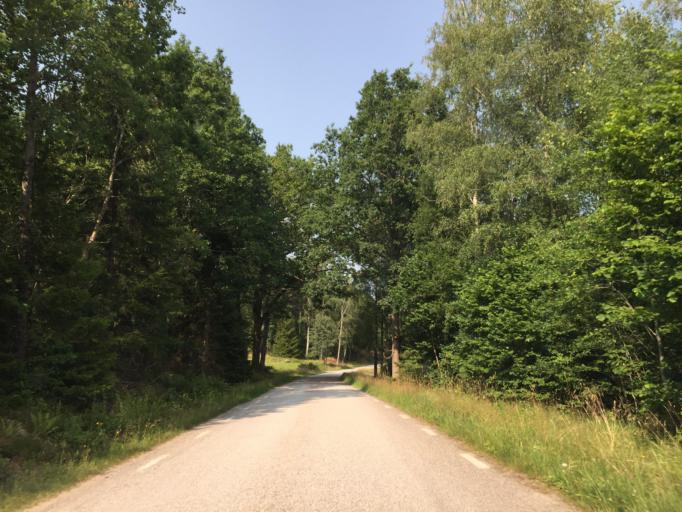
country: SE
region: Vaestra Goetaland
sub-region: Trollhattan
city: Sjuntorp
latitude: 58.2843
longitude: 12.1244
